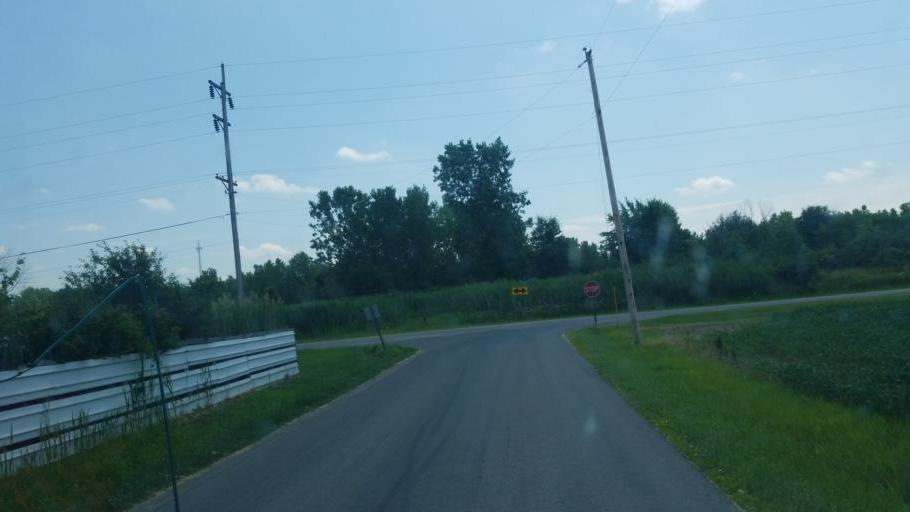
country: US
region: Ohio
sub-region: Crawford County
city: Crestline
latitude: 40.7852
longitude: -82.7652
